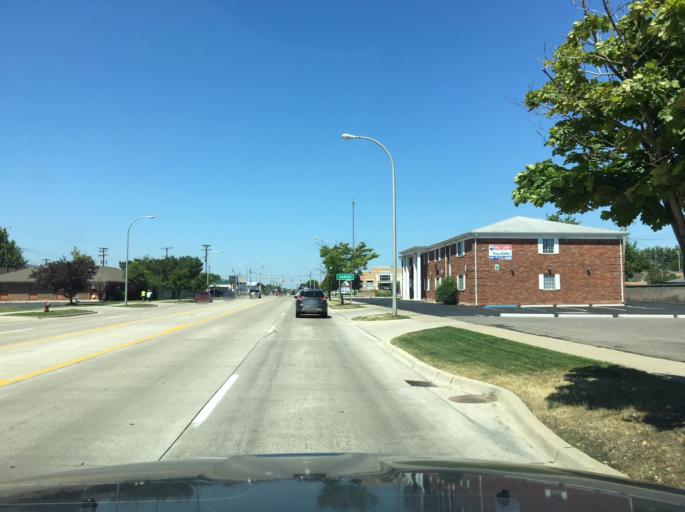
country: US
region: Michigan
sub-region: Wayne County
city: Grosse Pointe Woods
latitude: 42.4663
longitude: -82.9053
